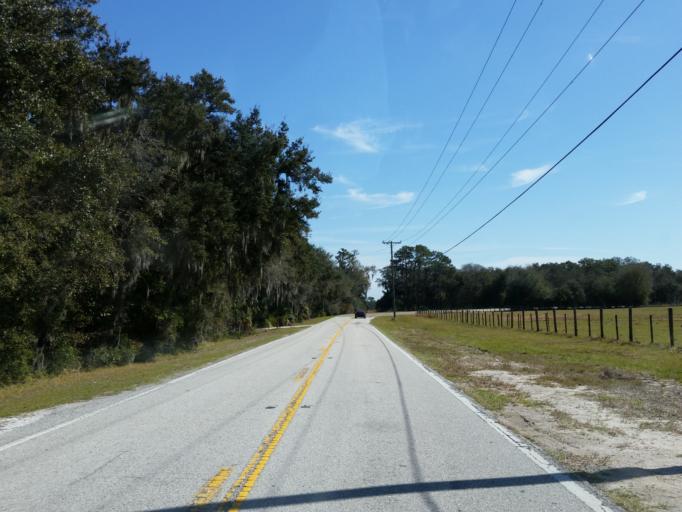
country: US
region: Florida
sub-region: Hillsborough County
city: Boyette
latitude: 27.8213
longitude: -82.2341
